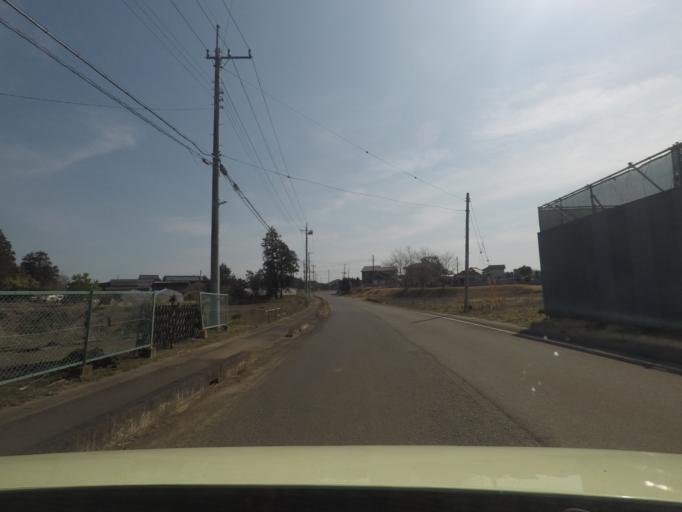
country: JP
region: Ibaraki
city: Ishioka
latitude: 36.1998
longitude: 140.3225
